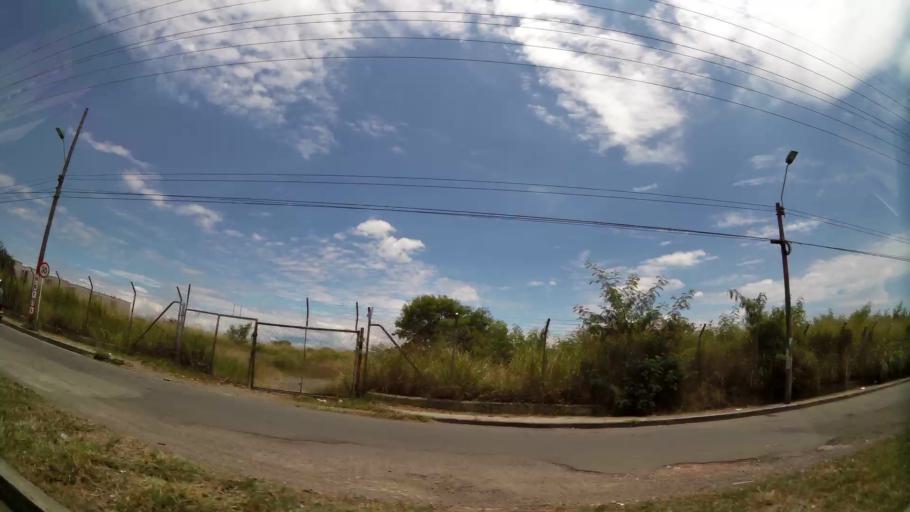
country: CO
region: Valle del Cauca
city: Cali
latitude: 3.4504
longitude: -76.4933
